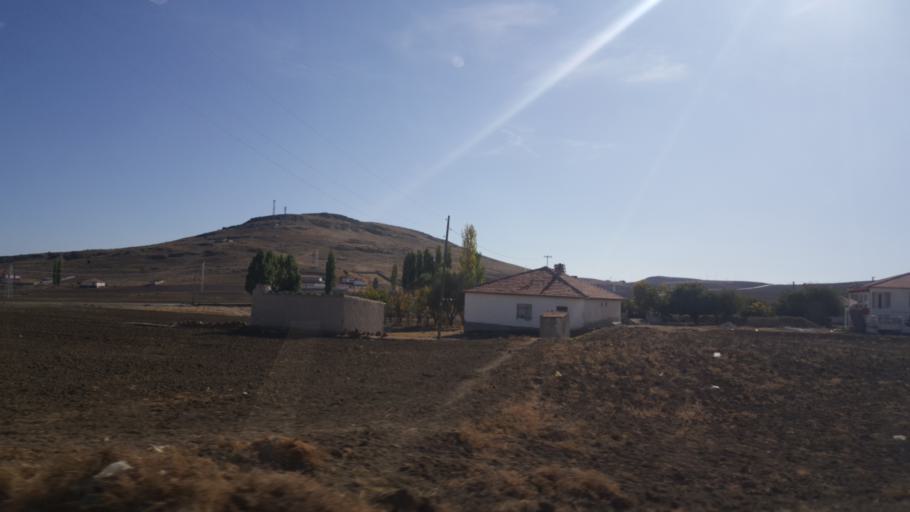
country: TR
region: Ankara
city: Yenice
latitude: 39.2735
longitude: 32.6687
